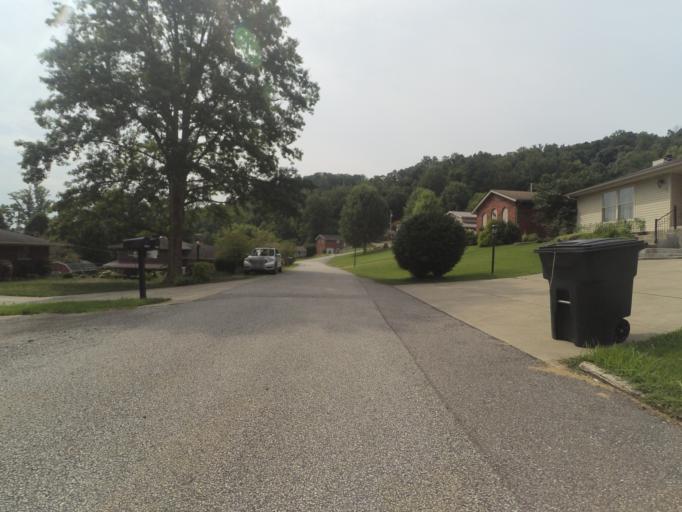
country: US
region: West Virginia
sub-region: Cabell County
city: Huntington
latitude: 38.4340
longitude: -82.4658
